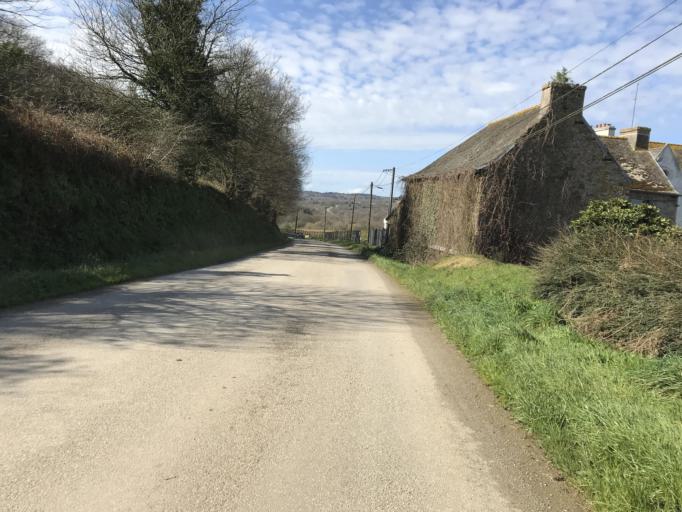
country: FR
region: Brittany
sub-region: Departement du Finistere
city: Loperhet
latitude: 48.3758
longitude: -4.2868
